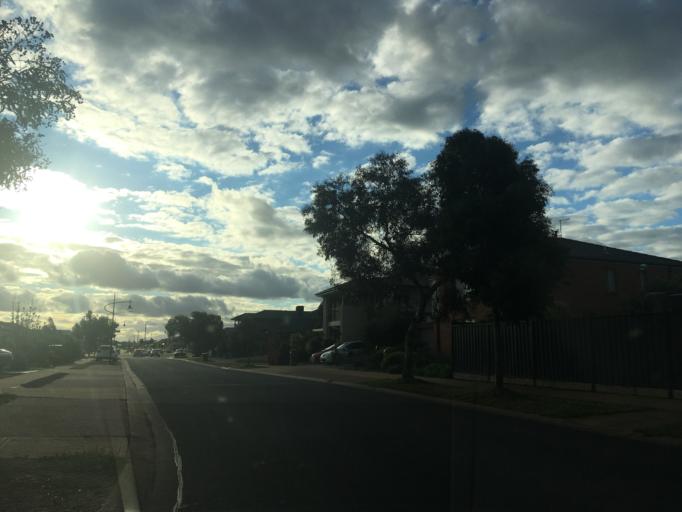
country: AU
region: Victoria
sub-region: Wyndham
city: Hoppers Crossing
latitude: -37.8925
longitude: 144.7192
